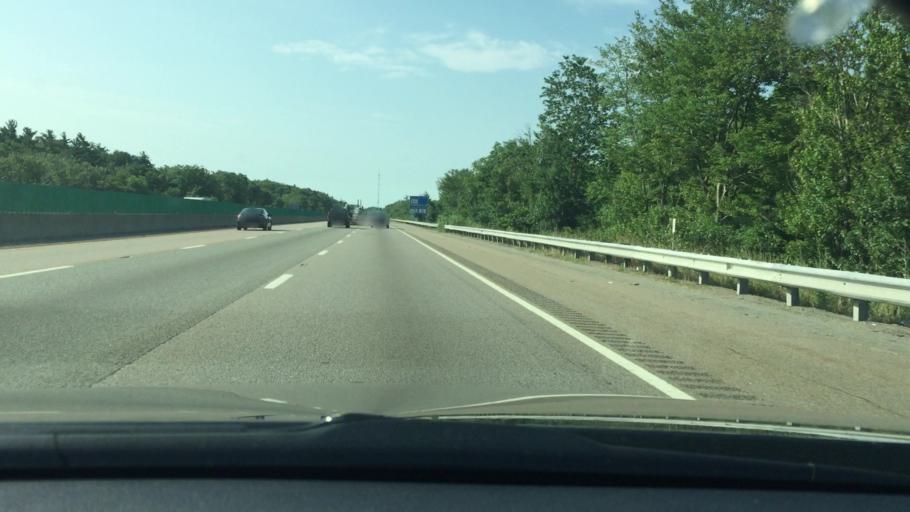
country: US
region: Massachusetts
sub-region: Plymouth County
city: West Bridgewater
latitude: 42.0389
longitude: -71.0540
